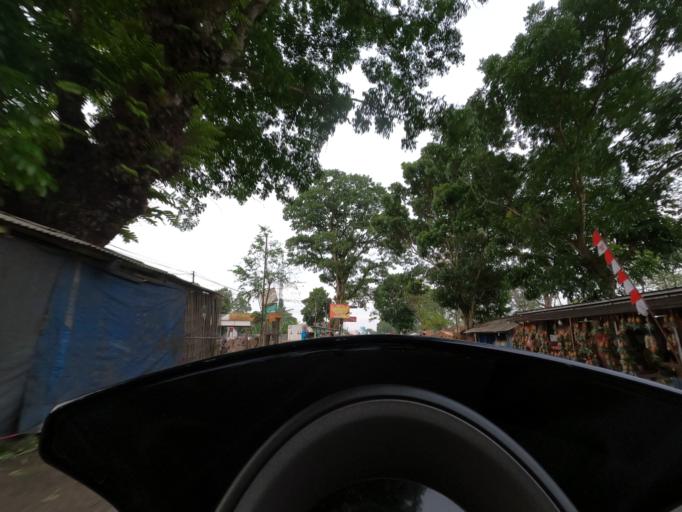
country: ID
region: West Java
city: Lembang
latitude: -6.6714
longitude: 107.6982
